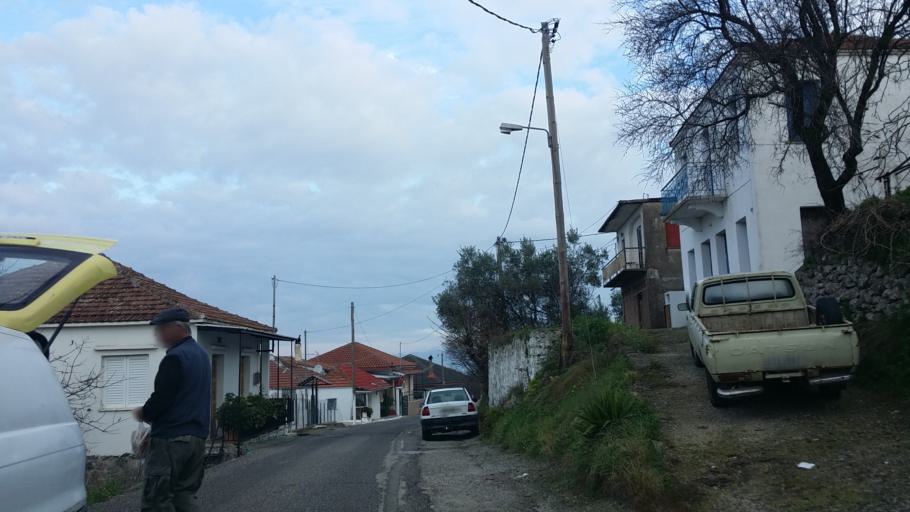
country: GR
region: West Greece
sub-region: Nomos Aitolias kai Akarnanias
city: Fitiai
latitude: 38.7088
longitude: 21.1698
